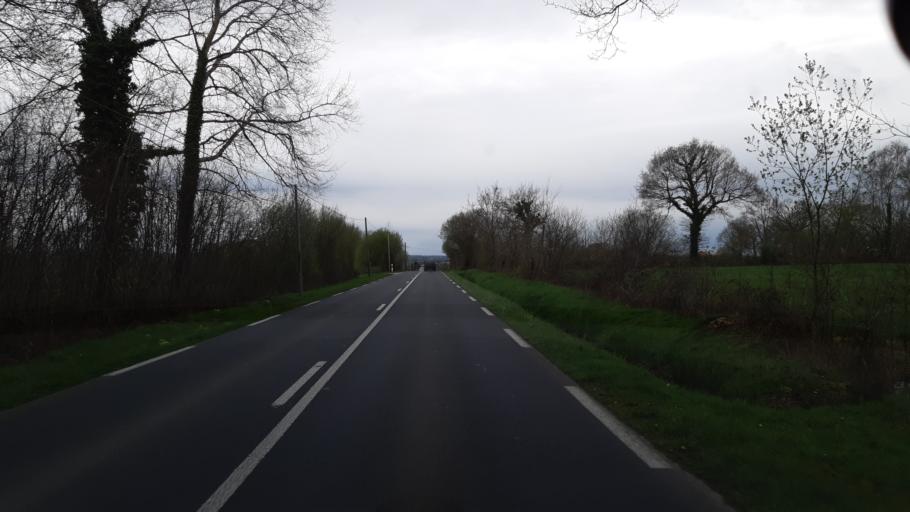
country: FR
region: Lower Normandy
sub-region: Departement de la Manche
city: Tessy-sur-Vire
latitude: 49.0165
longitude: -1.1483
